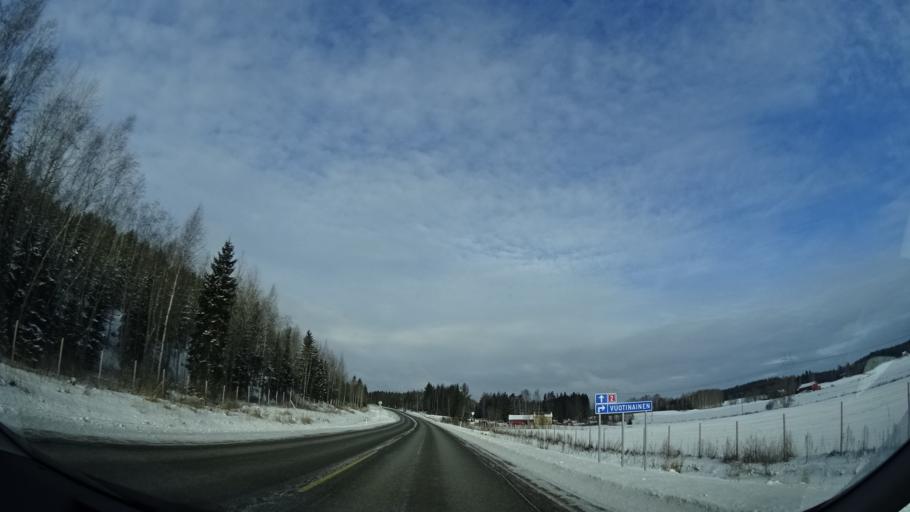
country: FI
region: Uusimaa
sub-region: Helsinki
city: Karkkila
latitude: 60.5832
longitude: 24.1291
